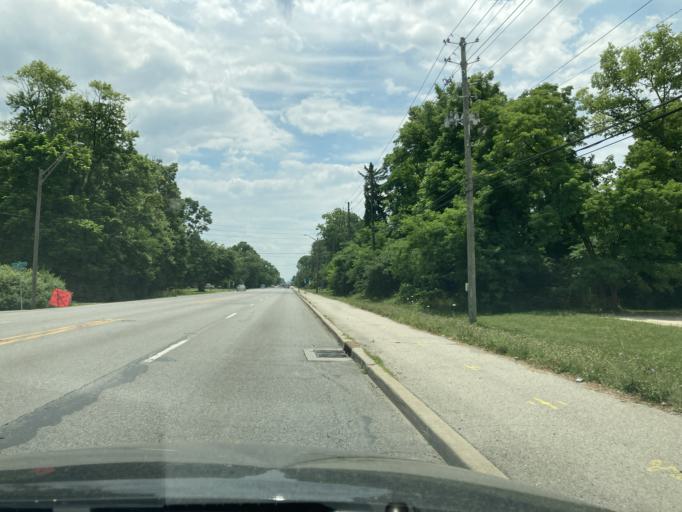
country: US
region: Indiana
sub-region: Marion County
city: Meridian Hills
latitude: 39.8784
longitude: -86.2068
